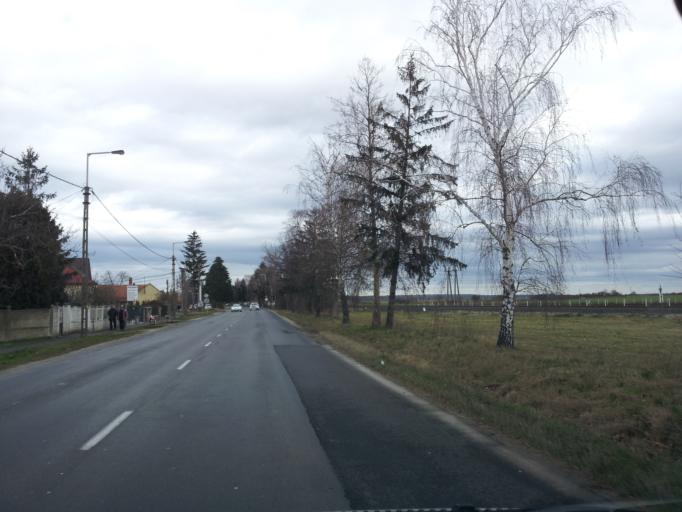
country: HU
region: Vas
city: Gencsapati
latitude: 47.3209
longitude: 16.5865
